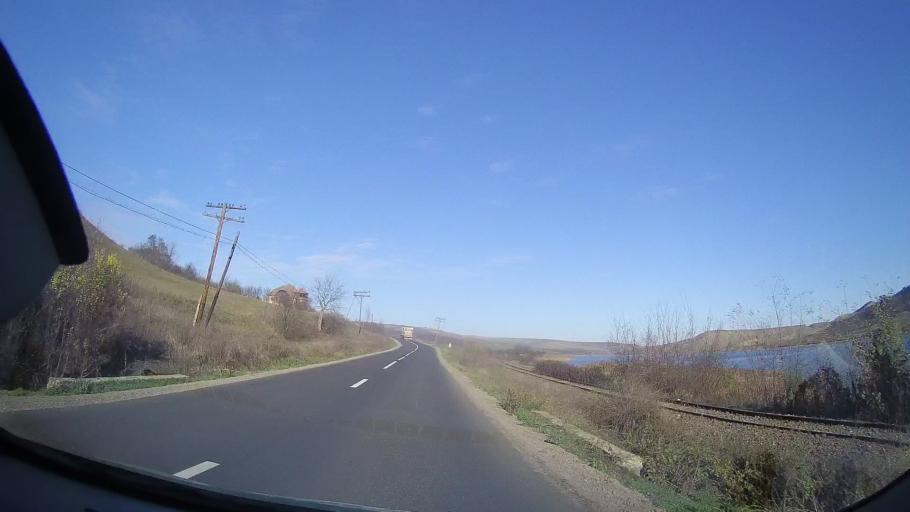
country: RO
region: Mures
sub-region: Comuna Zau De Campie
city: Zau de Campie
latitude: 46.6250
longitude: 24.1327
